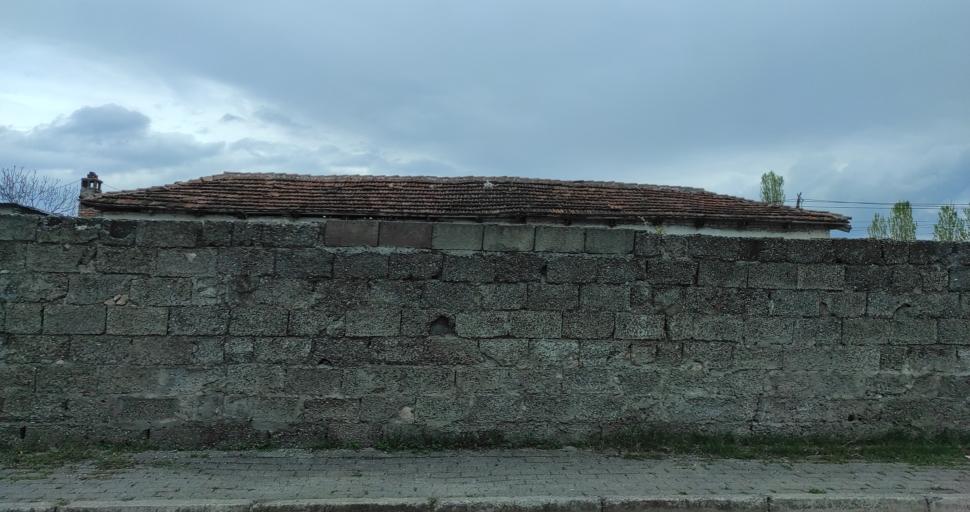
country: AL
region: Shkoder
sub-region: Rrethi i Shkodres
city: Berdica e Madhe
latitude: 41.9815
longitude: 19.4819
